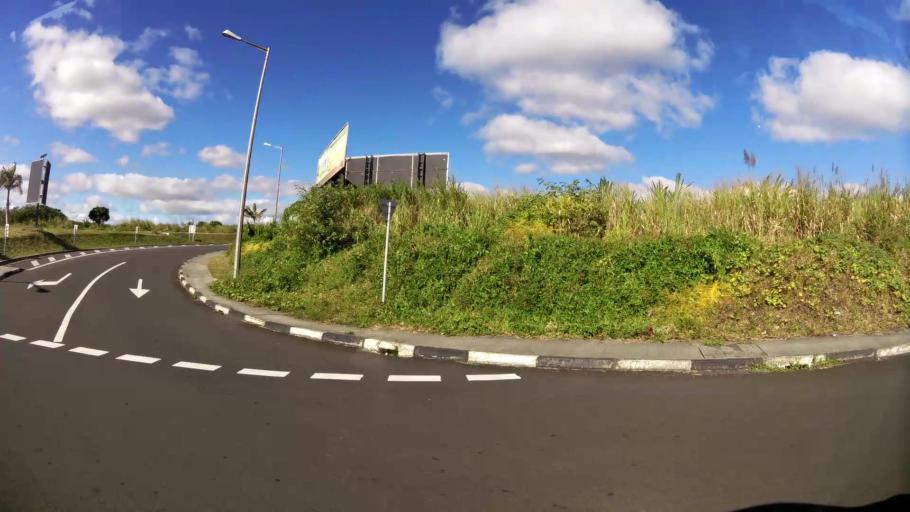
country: MU
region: Plaines Wilhems
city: Quatre Bornes
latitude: -20.2647
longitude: 57.4915
